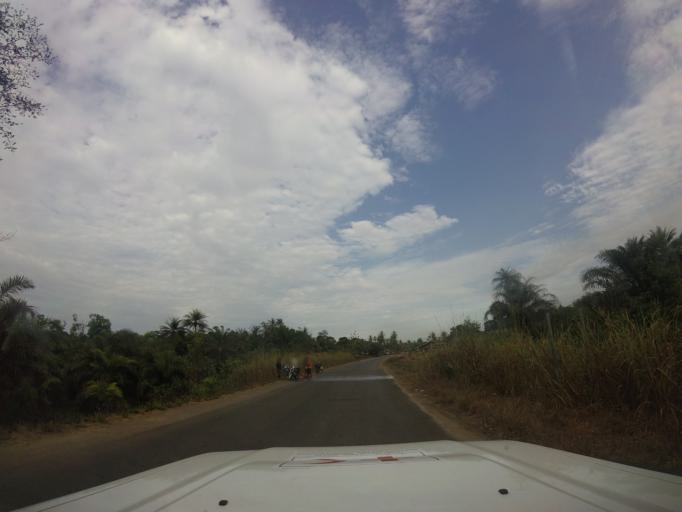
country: LR
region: Grand Cape Mount
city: Robertsport
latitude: 6.9298
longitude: -11.2503
